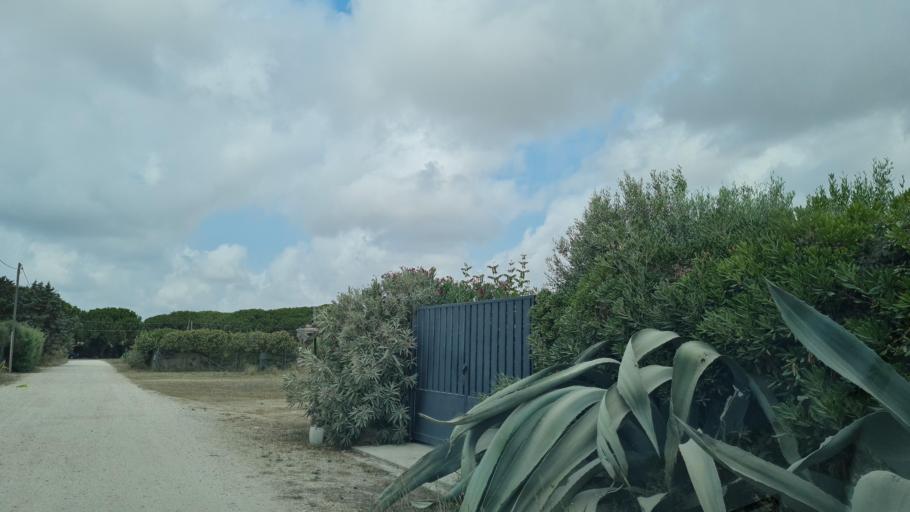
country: IT
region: Latium
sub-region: Provincia di Viterbo
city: Tarquinia
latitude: 42.1931
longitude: 11.7296
